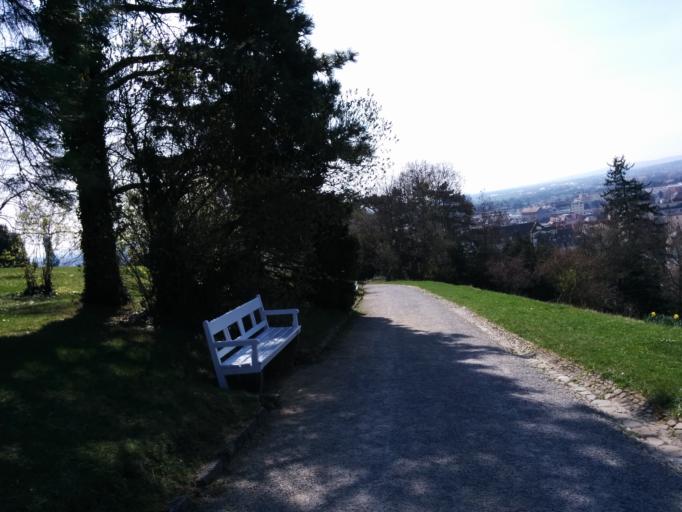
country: AT
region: Lower Austria
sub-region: Politischer Bezirk Baden
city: Baden
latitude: 48.0127
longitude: 16.2338
